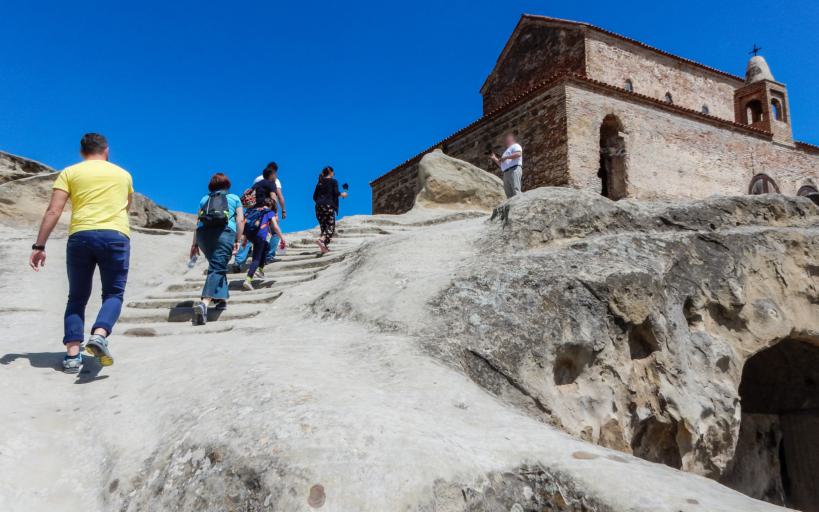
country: GE
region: Shida Kartli
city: Gori
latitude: 41.9673
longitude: 44.2073
